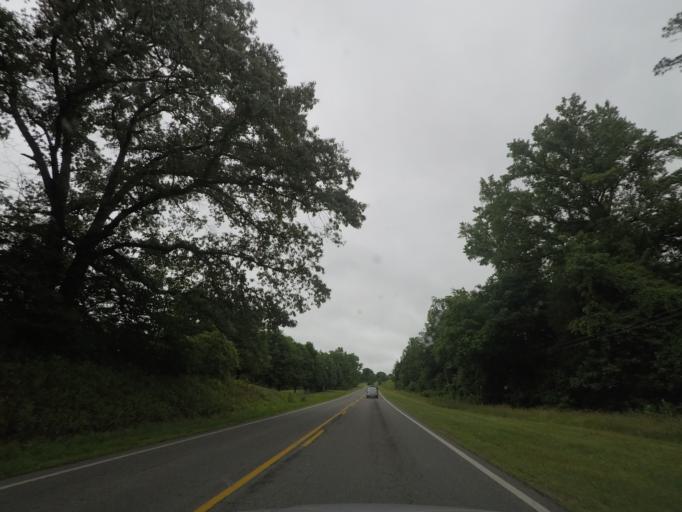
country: US
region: Virginia
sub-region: Fluvanna County
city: Palmyra
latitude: 37.8025
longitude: -78.2390
